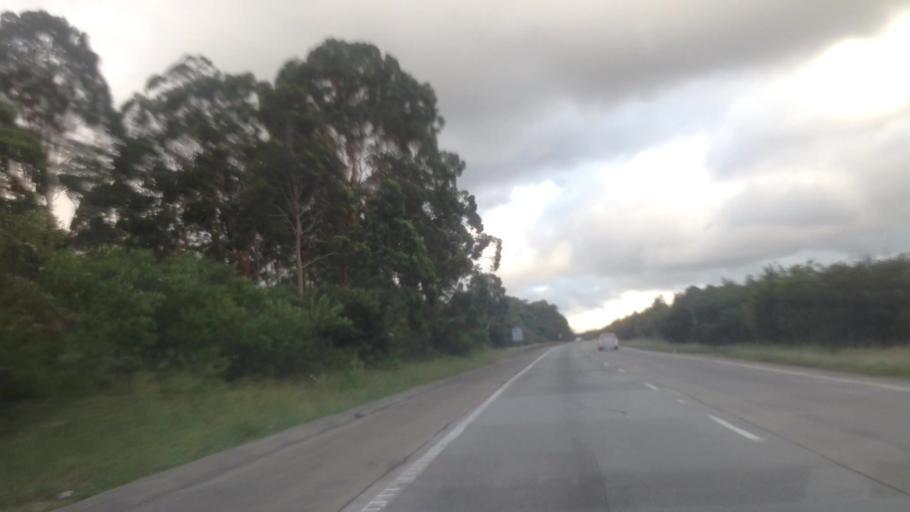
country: AU
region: New South Wales
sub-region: Wyong Shire
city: Jilliby
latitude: -33.2075
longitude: 151.4553
